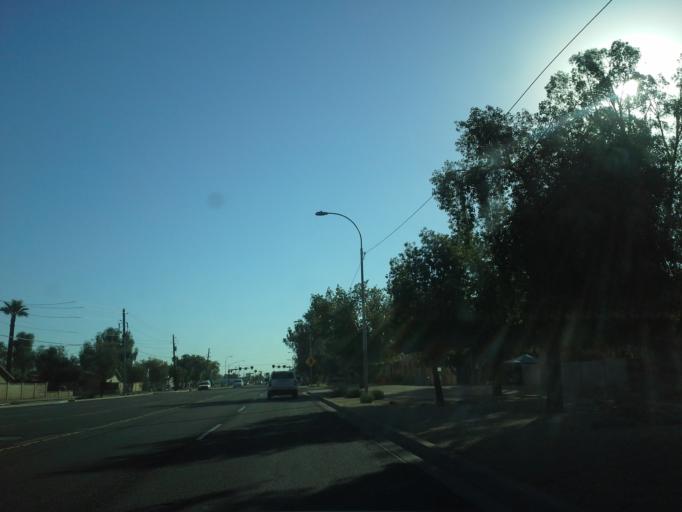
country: US
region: Arizona
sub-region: Maricopa County
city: Glendale
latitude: 33.4804
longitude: -112.1567
